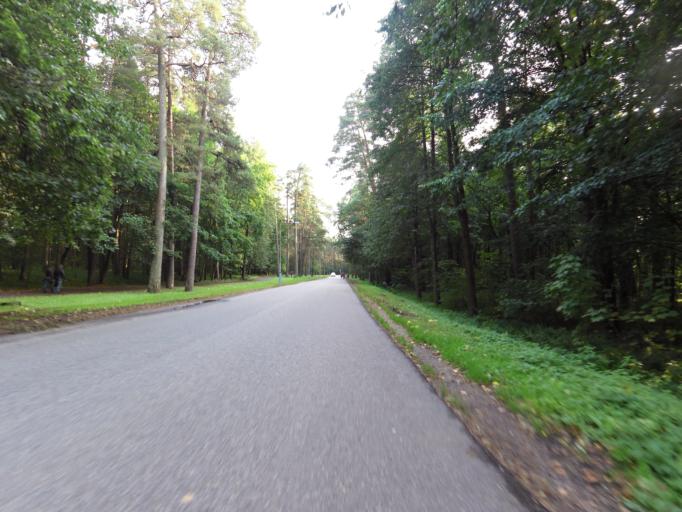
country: LT
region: Vilnius County
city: Vilkpede
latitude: 54.6800
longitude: 25.2342
